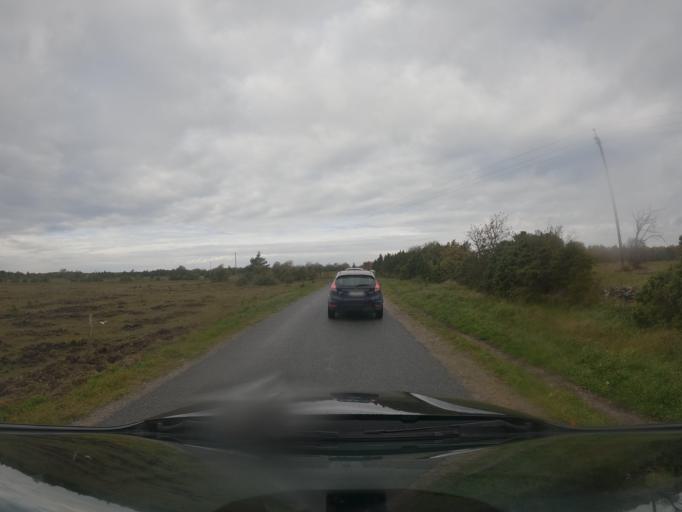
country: EE
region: Saare
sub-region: Kuressaare linn
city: Kuressaare
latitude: 58.4447
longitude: 21.9766
